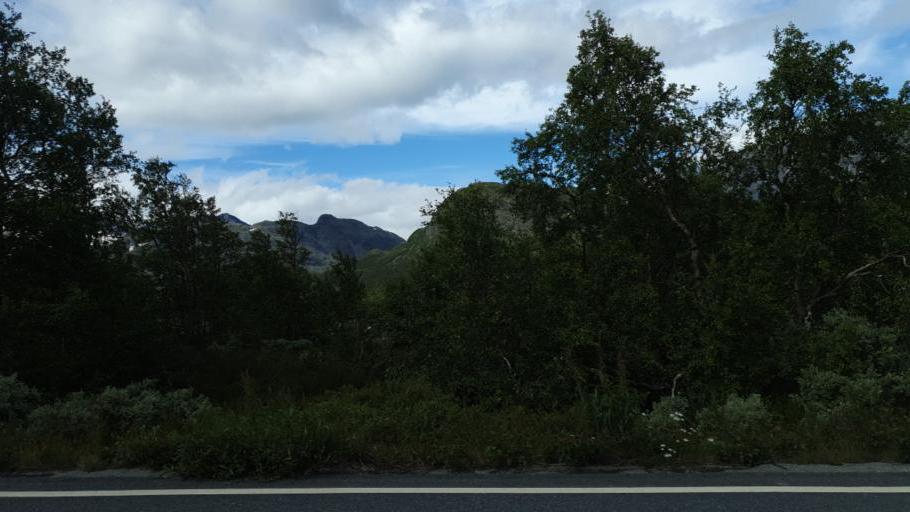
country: NO
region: Oppland
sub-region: Oystre Slidre
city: Heggenes
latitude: 61.4834
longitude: 8.8370
